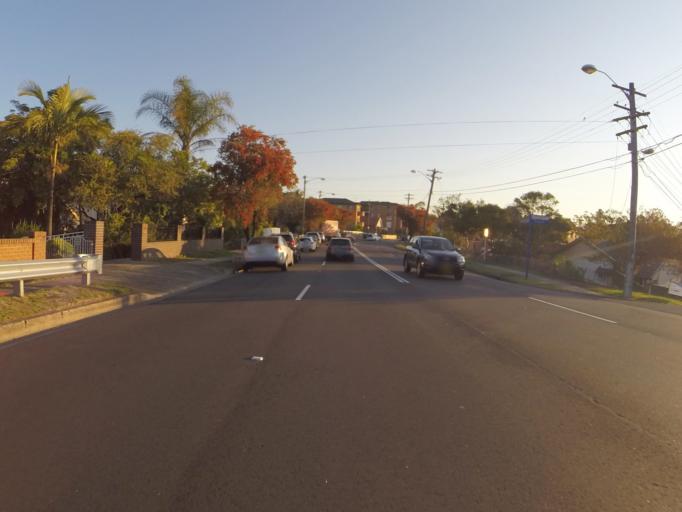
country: AU
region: New South Wales
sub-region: Rockdale
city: Bardwell Valley
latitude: -33.9242
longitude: 151.1352
